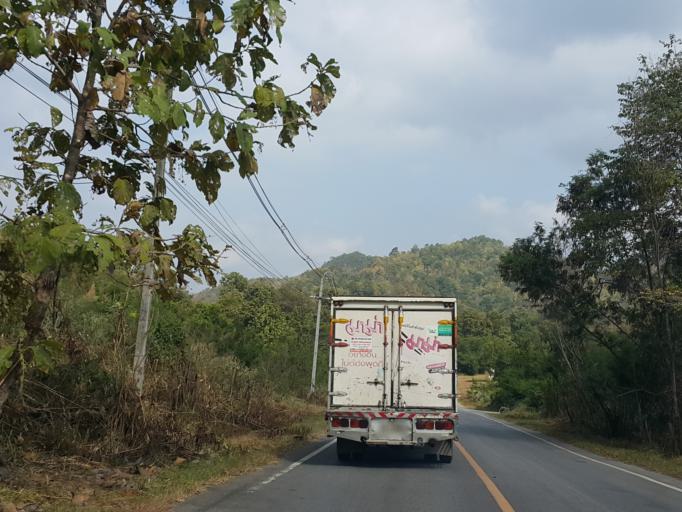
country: TH
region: Chiang Mai
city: Mae On
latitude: 18.8191
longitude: 99.2585
